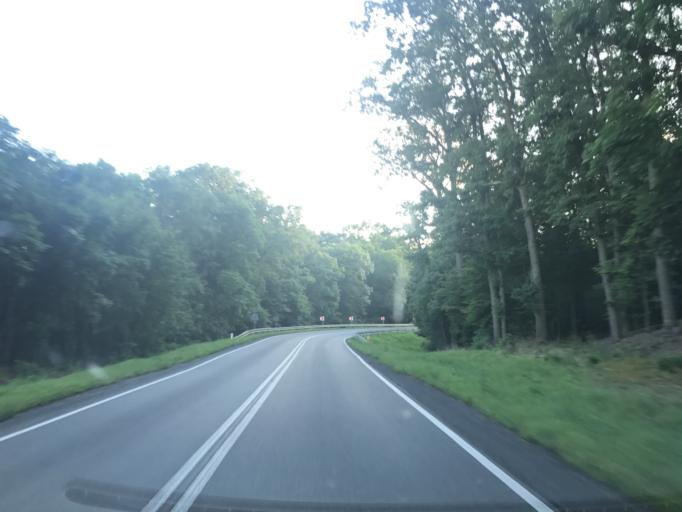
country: PL
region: Greater Poland Voivodeship
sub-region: Powiat gostynski
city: Piaski
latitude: 51.8966
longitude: 17.1310
